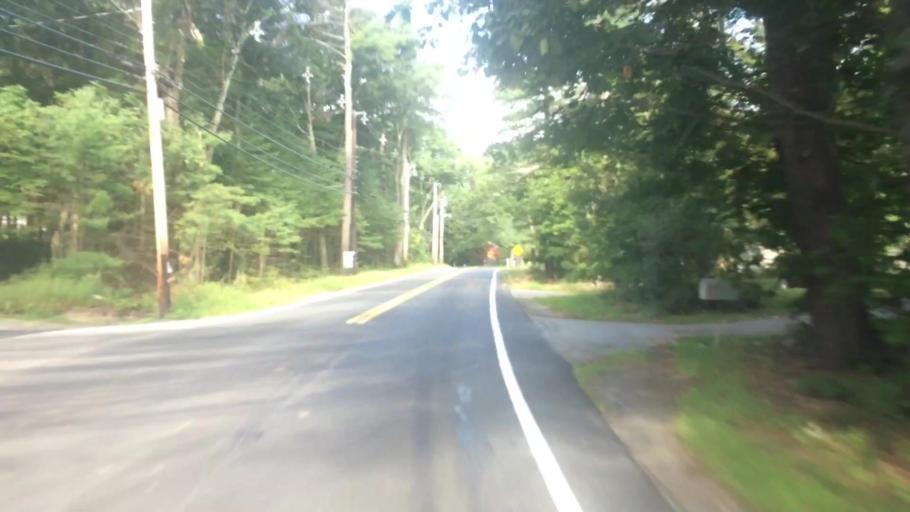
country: US
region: Massachusetts
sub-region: Middlesex County
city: Stow
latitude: 42.4800
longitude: -71.4977
